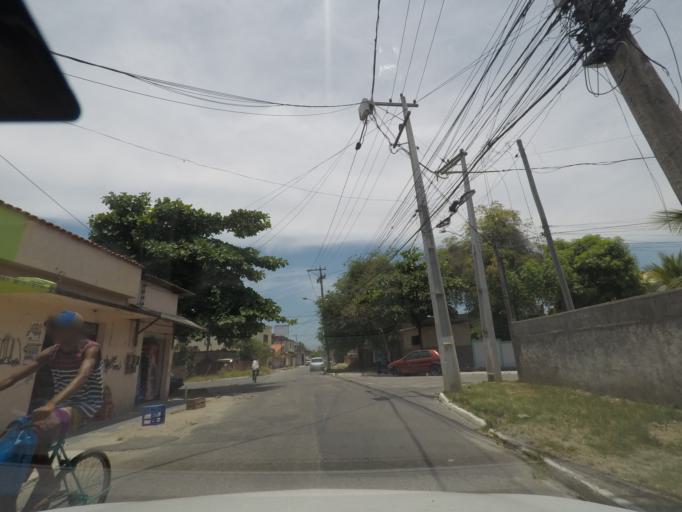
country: BR
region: Rio de Janeiro
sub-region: Marica
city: Marica
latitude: -22.9104
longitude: -42.8392
